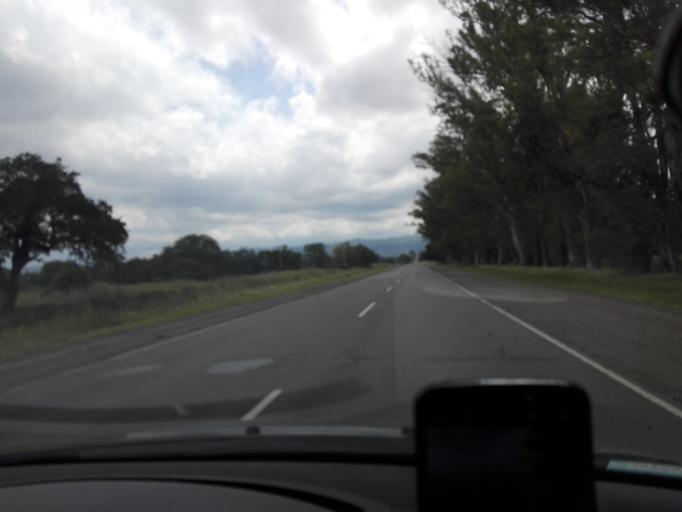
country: AR
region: Cordoba
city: Alta Gracia
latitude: -31.6582
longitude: -64.3876
